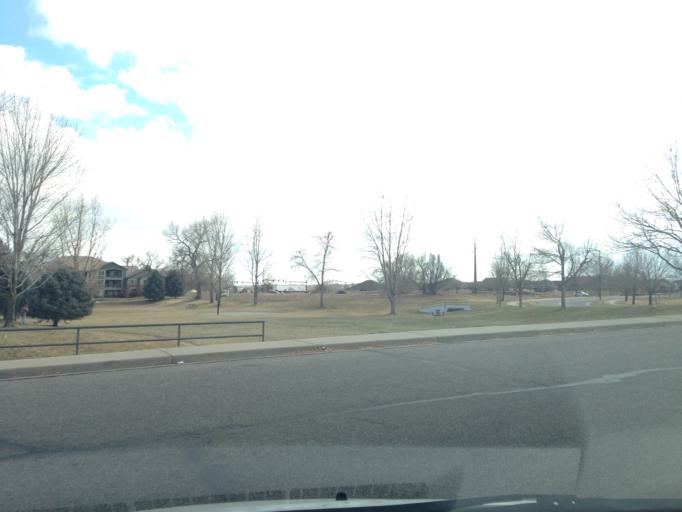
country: US
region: Colorado
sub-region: Boulder County
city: Lafayette
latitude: 39.9889
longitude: -105.0885
